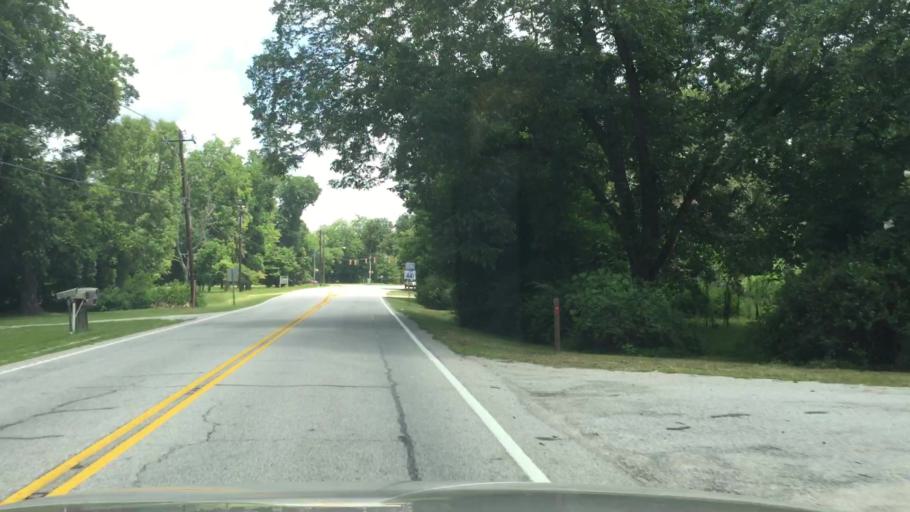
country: US
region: South Carolina
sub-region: Sumter County
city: South Sumter
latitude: 33.9141
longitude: -80.3907
